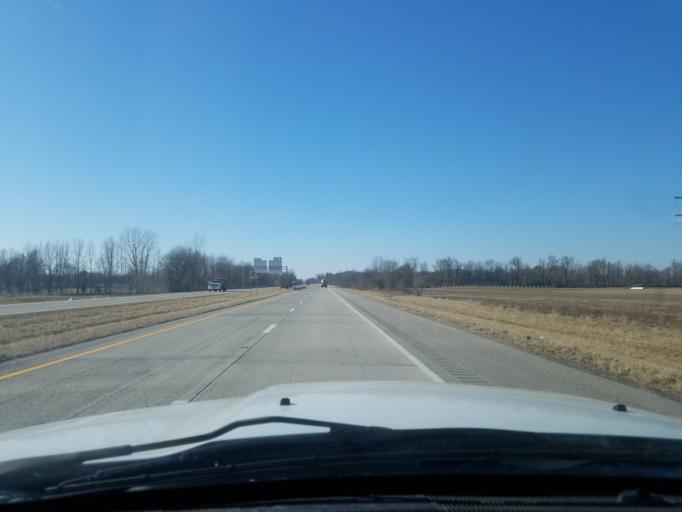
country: US
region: Kentucky
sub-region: Daviess County
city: Owensboro
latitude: 37.7672
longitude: -87.1857
